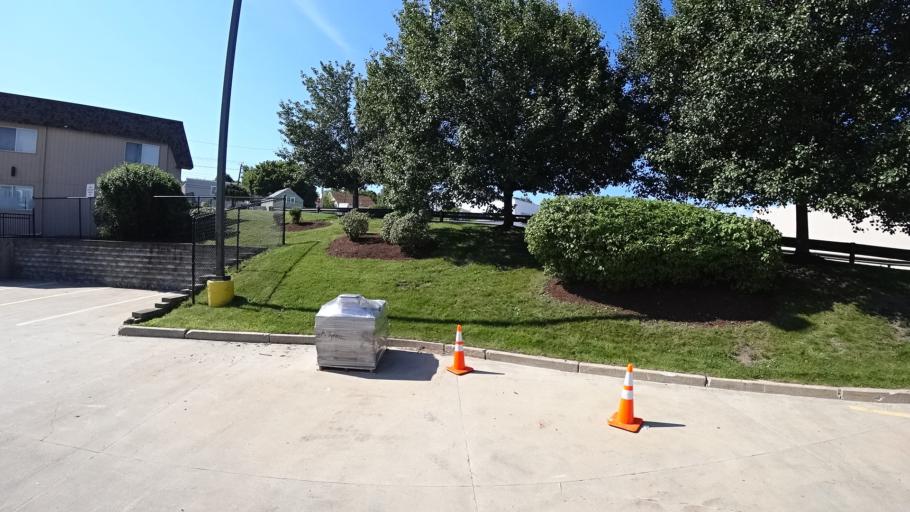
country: US
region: Massachusetts
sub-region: Norfolk County
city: Dedham
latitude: 42.2517
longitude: -71.1700
